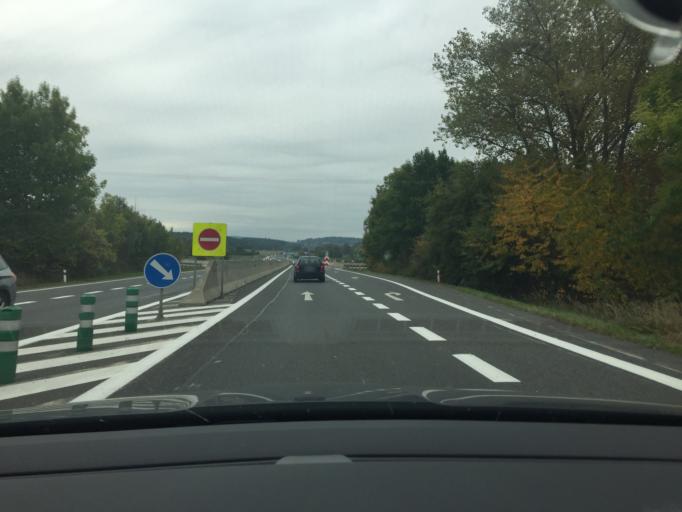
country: CZ
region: Jihocesky
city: Mirotice
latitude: 49.4144
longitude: 14.0372
